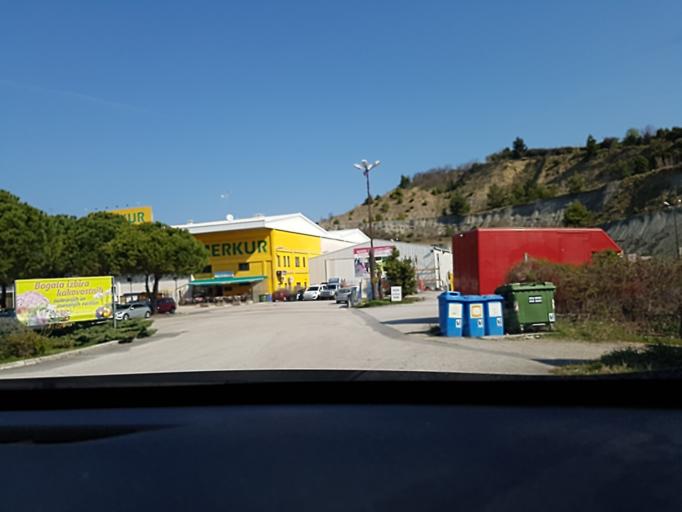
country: SI
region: Izola-Isola
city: Izola
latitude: 45.5421
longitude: 13.6775
